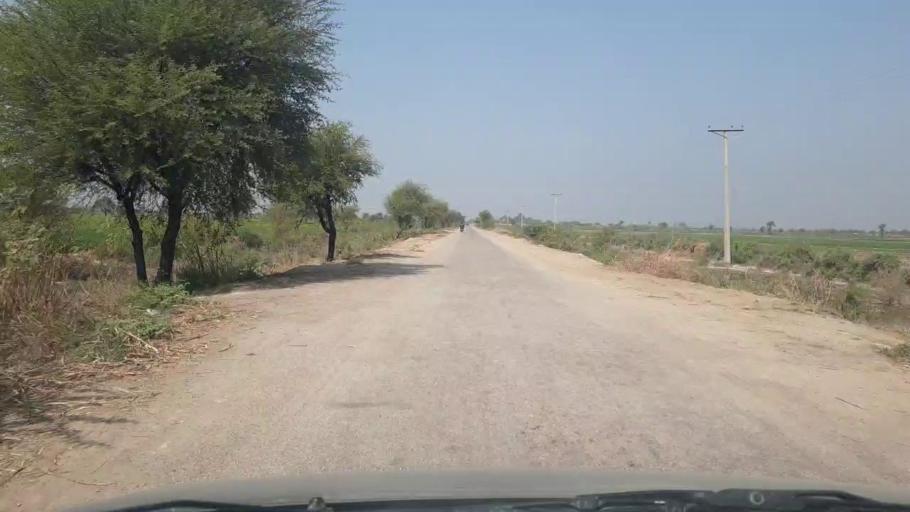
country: PK
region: Sindh
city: Mirwah Gorchani
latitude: 25.3228
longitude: 69.1513
